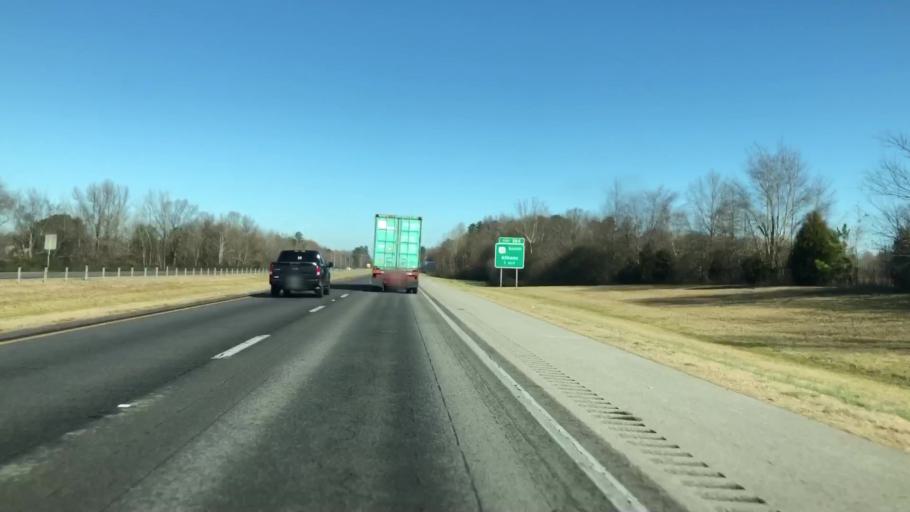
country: US
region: Alabama
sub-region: Limestone County
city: Athens
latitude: 34.8156
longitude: -86.9386
